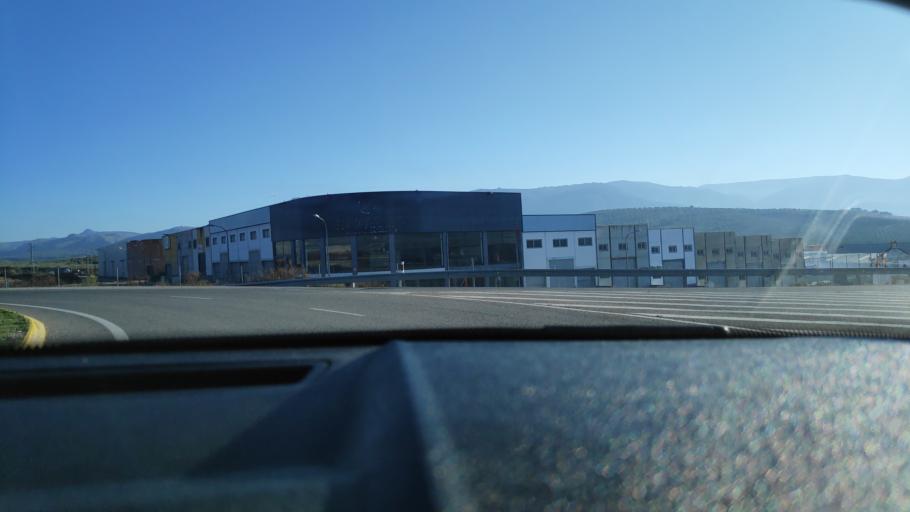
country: ES
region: Andalusia
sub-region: Province of Cordoba
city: Baena
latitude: 37.5952
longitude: -4.3030
